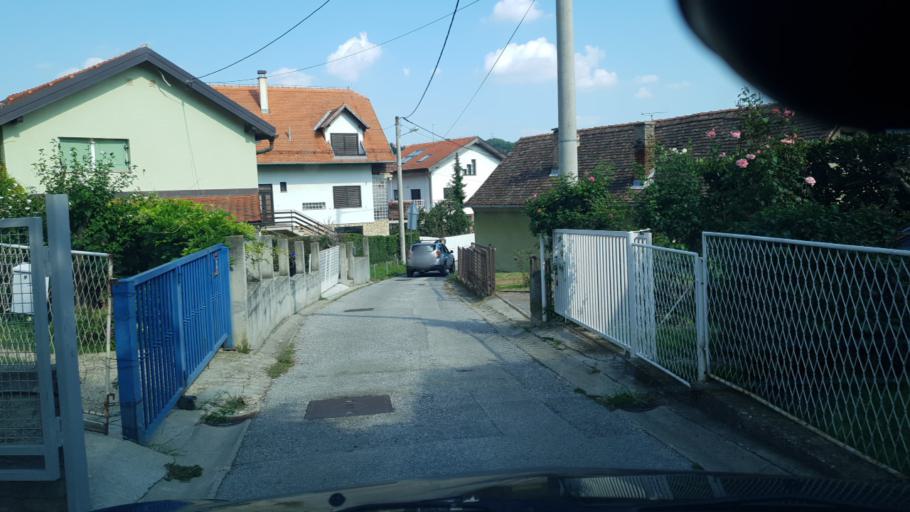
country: HR
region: Grad Zagreb
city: Zagreb
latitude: 45.8591
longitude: 15.9692
